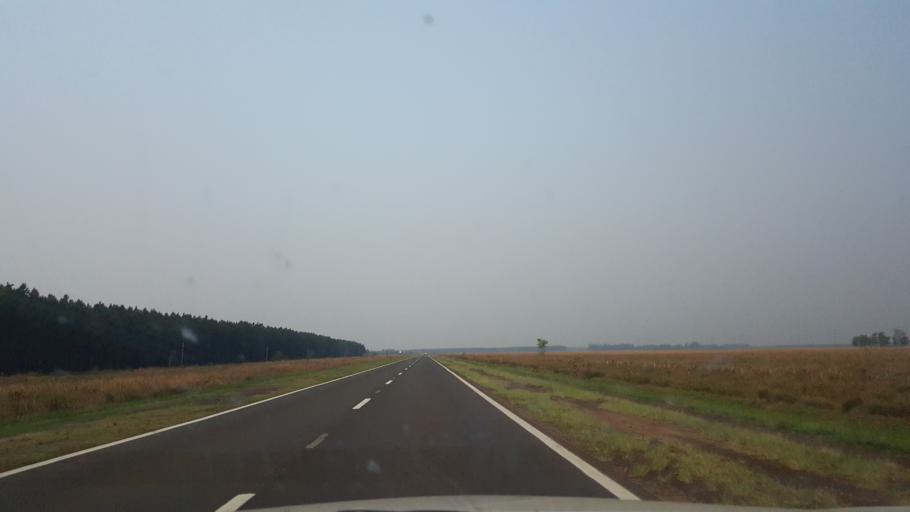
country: AR
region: Corrientes
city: Ituzaingo
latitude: -27.6332
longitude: -56.8975
